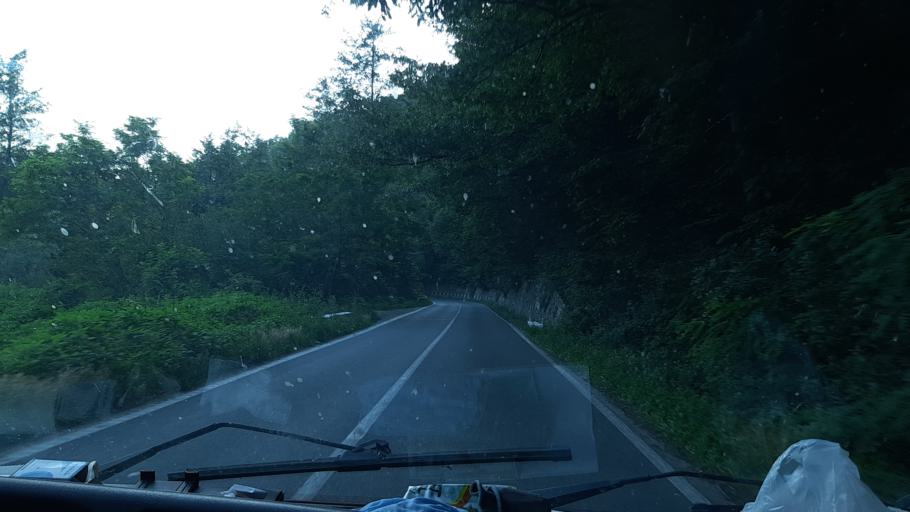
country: RO
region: Caras-Severin
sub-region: Municipiul Resita
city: Calnic
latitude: 45.3683
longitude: 21.8178
